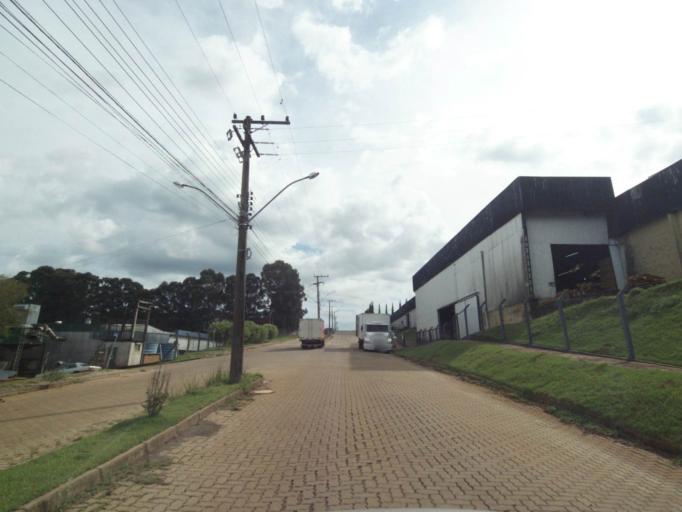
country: BR
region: Rio Grande do Sul
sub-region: Lagoa Vermelha
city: Lagoa Vermelha
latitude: -28.2282
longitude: -51.5124
